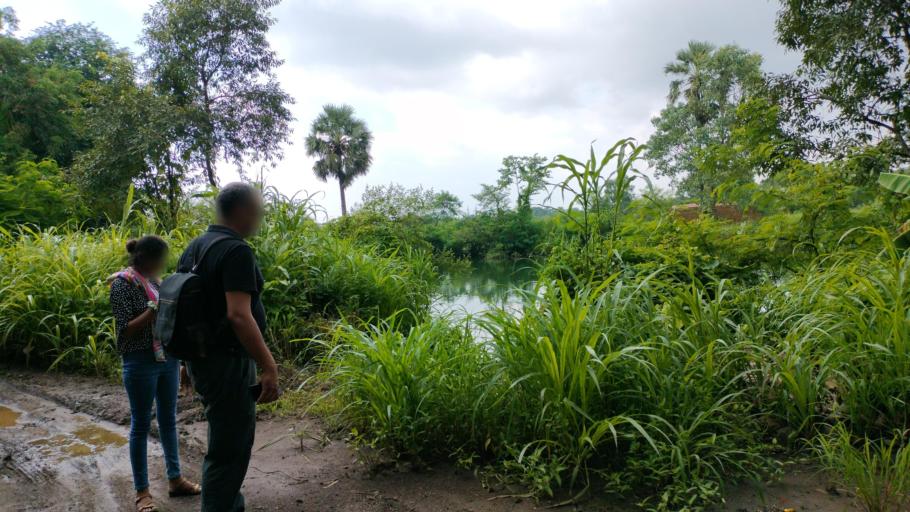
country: IN
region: Maharashtra
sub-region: Thane
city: Virar
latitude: 19.4735
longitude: 72.8560
